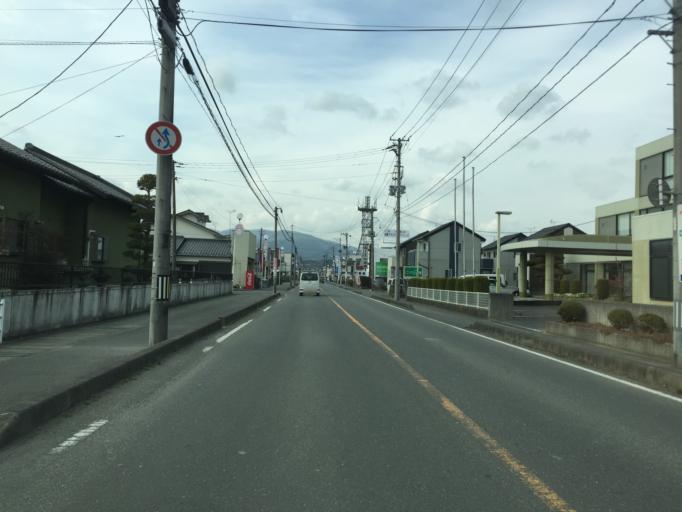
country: JP
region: Ibaraki
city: Kitaibaraki
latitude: 36.8879
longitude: 140.7720
